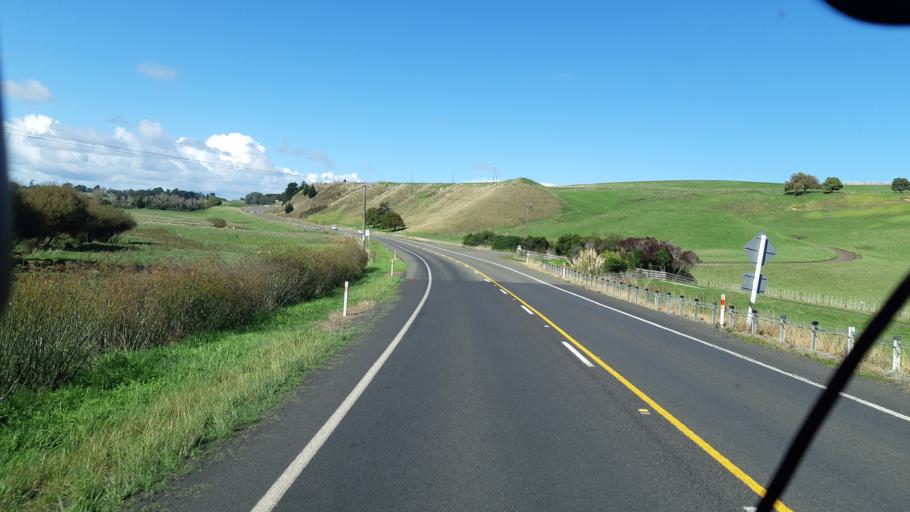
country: NZ
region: Manawatu-Wanganui
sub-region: Wanganui District
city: Wanganui
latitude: -39.9667
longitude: 175.1018
